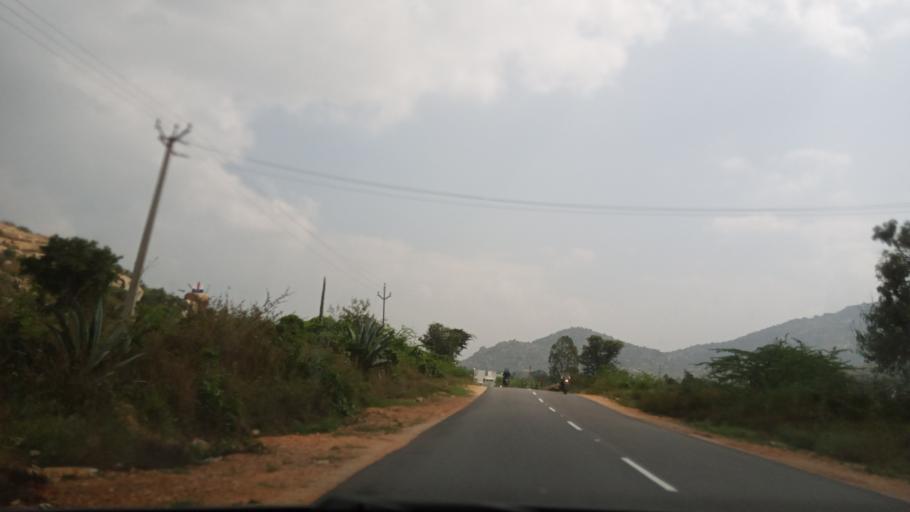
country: IN
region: Andhra Pradesh
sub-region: Chittoor
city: Madanapalle
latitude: 13.6350
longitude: 78.6150
